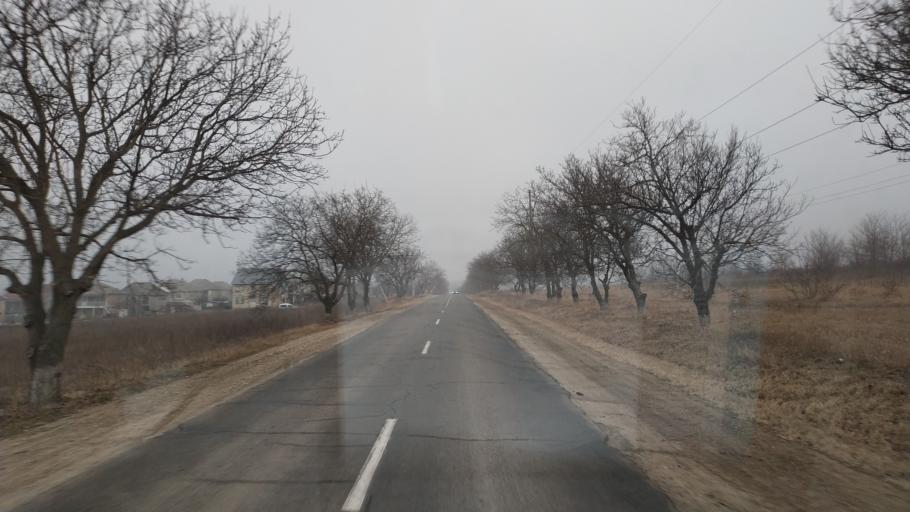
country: MD
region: Laloveni
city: Ialoveni
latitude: 46.9370
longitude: 28.7998
